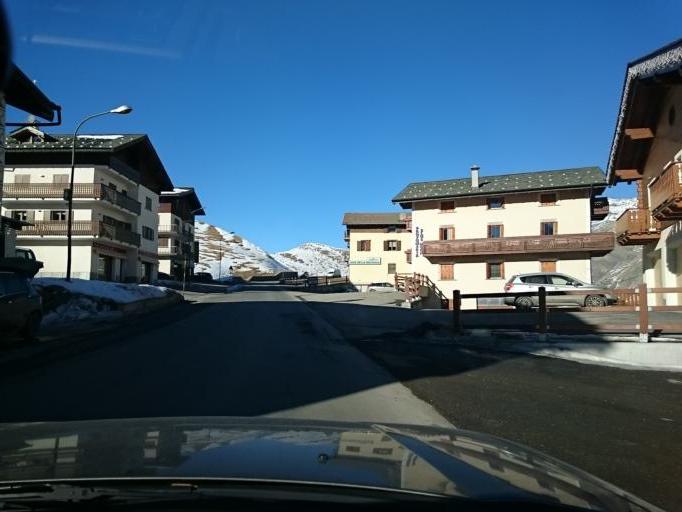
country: IT
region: Lombardy
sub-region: Provincia di Sondrio
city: Livigno
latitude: 46.5200
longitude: 10.1790
